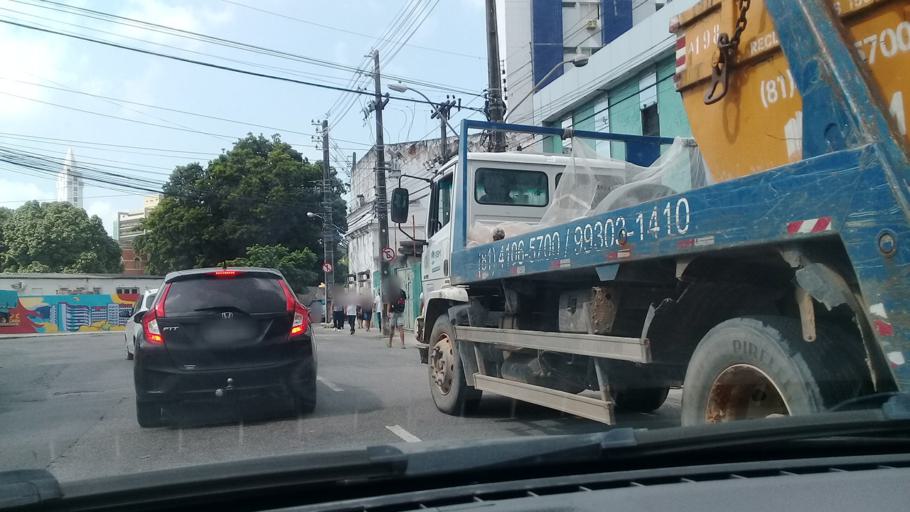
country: BR
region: Pernambuco
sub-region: Recife
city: Recife
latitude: -8.0546
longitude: -34.8897
